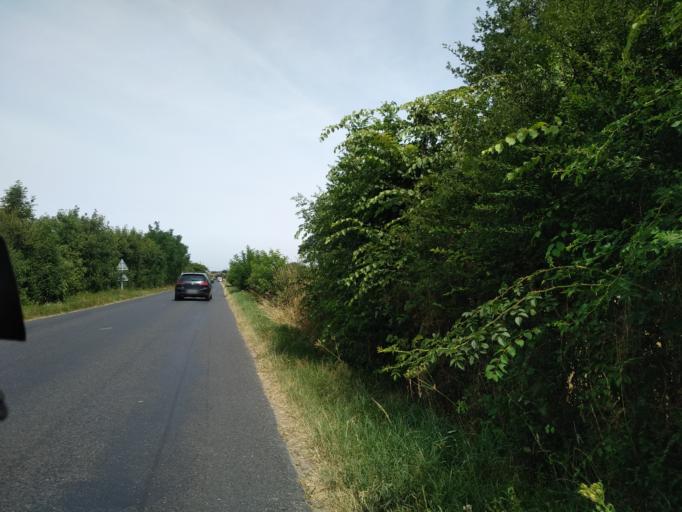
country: FR
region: Bourgogne
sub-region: Departement de Saone-et-Loire
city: Digoin
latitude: 46.4480
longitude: 3.9708
